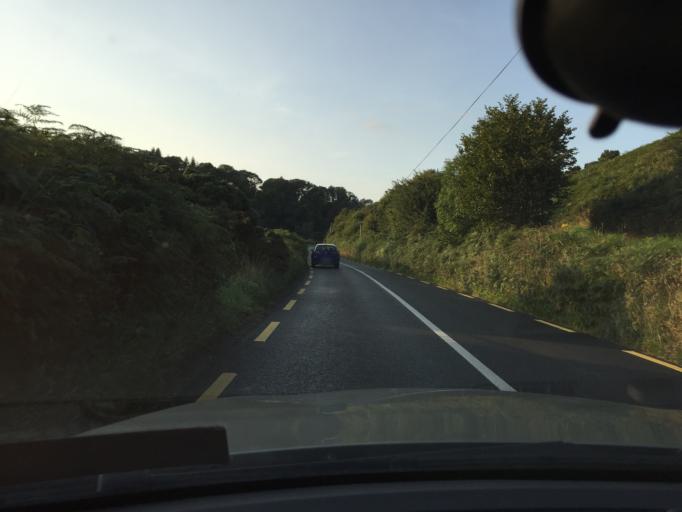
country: IE
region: Leinster
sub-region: Wicklow
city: Rathdrum
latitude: 53.0365
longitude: -6.2493
